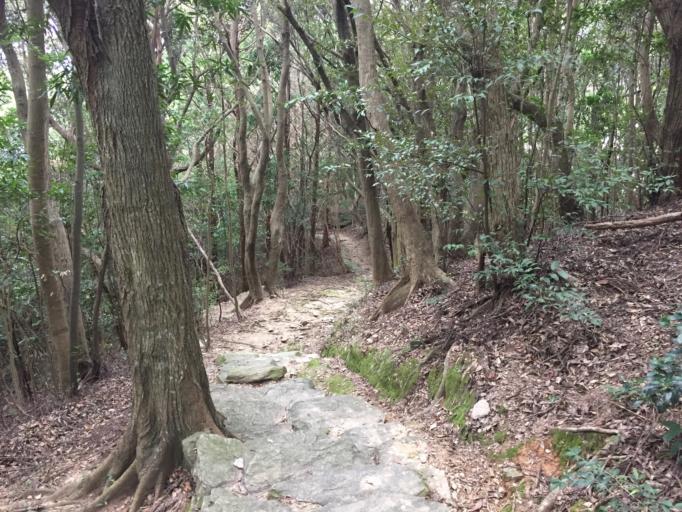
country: JP
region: Nagasaki
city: Togitsu
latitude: 32.8393
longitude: 129.7232
